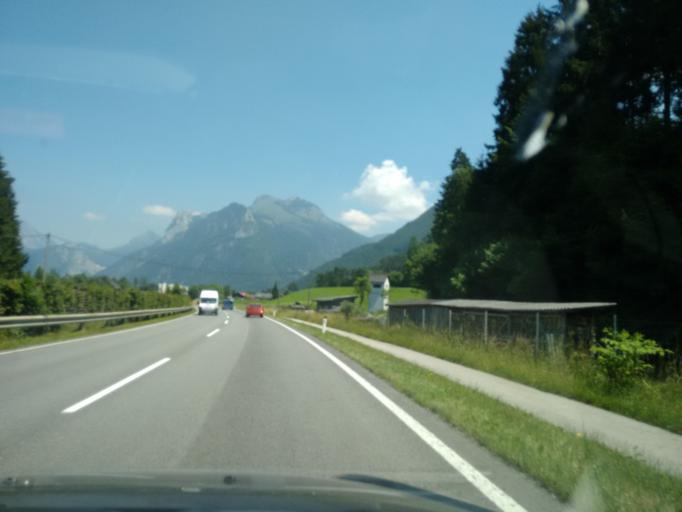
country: AT
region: Upper Austria
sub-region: Politischer Bezirk Gmunden
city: Ebensee
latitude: 47.7901
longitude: 13.7618
